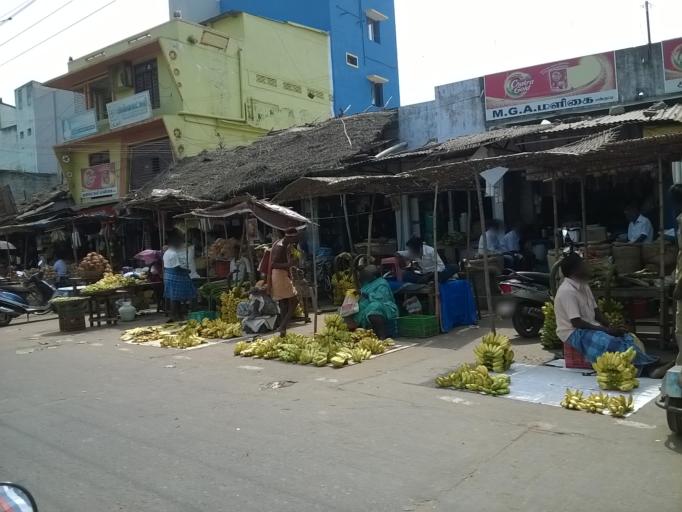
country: IN
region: Tamil Nadu
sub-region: Cuddalore
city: Panruti
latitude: 11.7733
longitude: 79.5510
